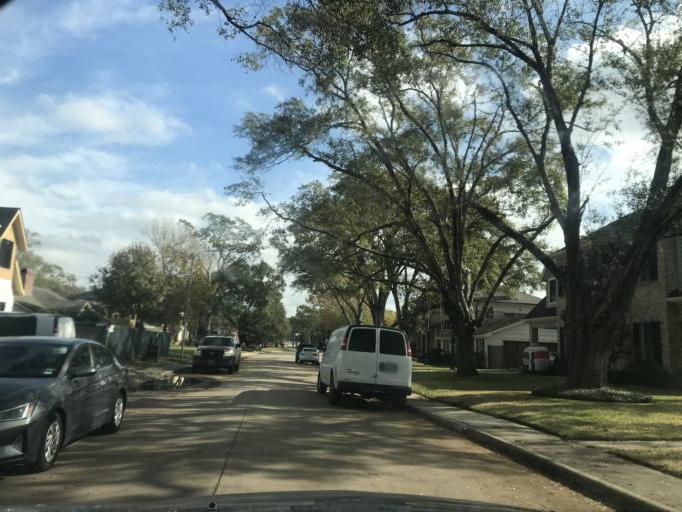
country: US
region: Texas
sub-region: Harris County
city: Hunters Creek Village
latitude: 29.7417
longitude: -95.4938
